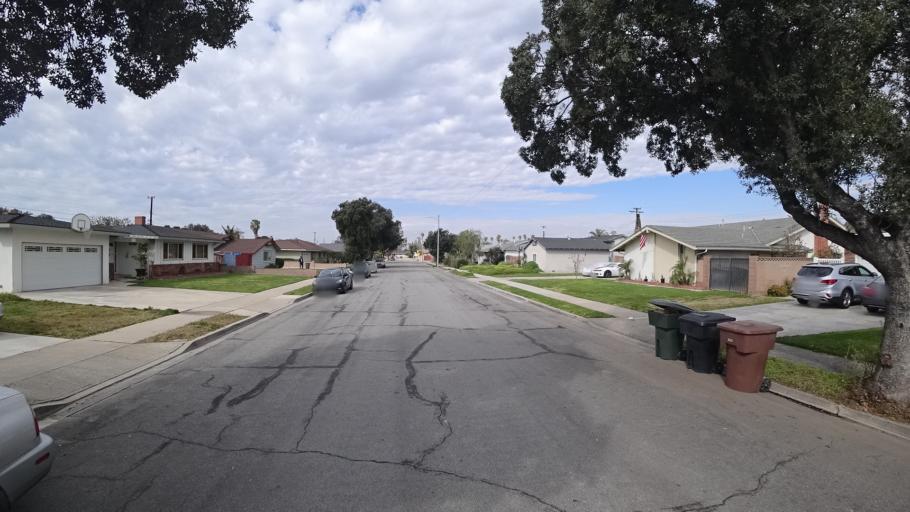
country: US
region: California
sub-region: Orange County
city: Placentia
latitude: 33.8495
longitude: -117.8841
